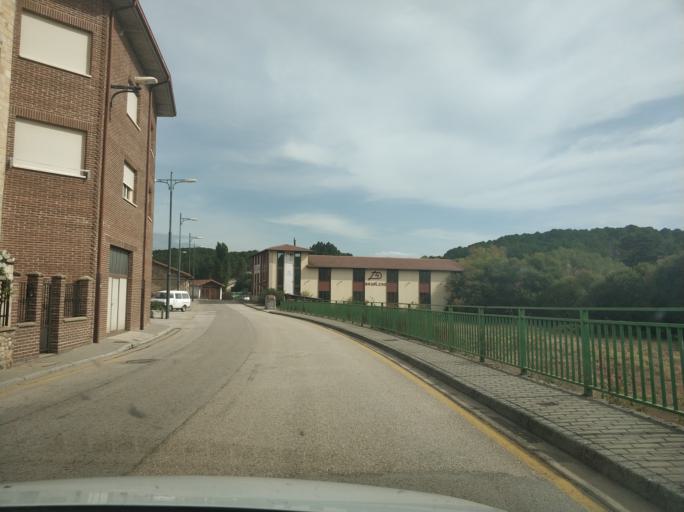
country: ES
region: Castille and Leon
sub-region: Provincia de Soria
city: Navaleno
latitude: 41.8387
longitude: -3.0022
